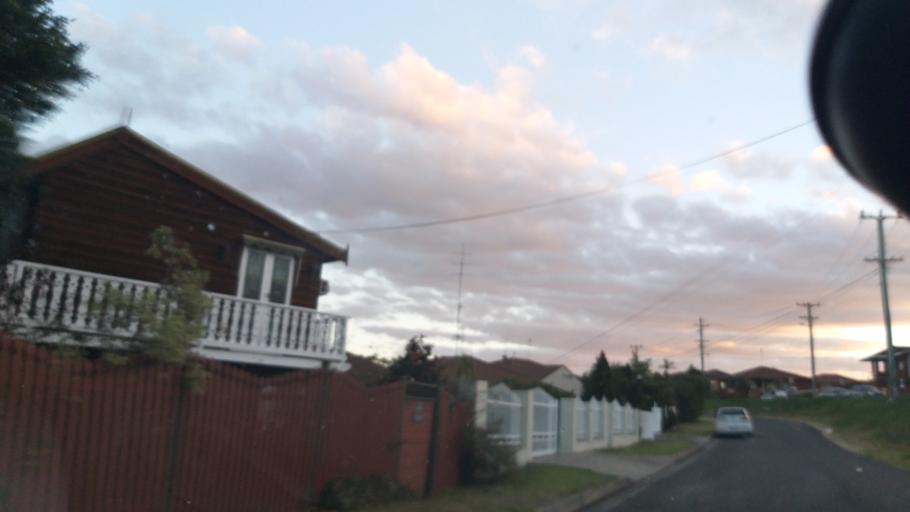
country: AU
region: New South Wales
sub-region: Wollongong
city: Lake Heights
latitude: -34.4826
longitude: 150.8790
